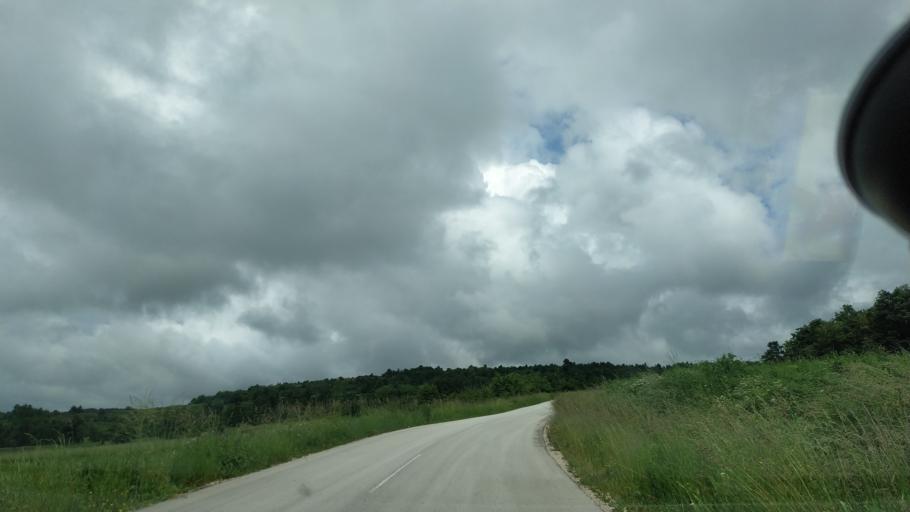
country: RS
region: Central Serbia
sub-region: Zajecarski Okrug
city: Soko Banja
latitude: 43.6861
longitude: 21.9311
